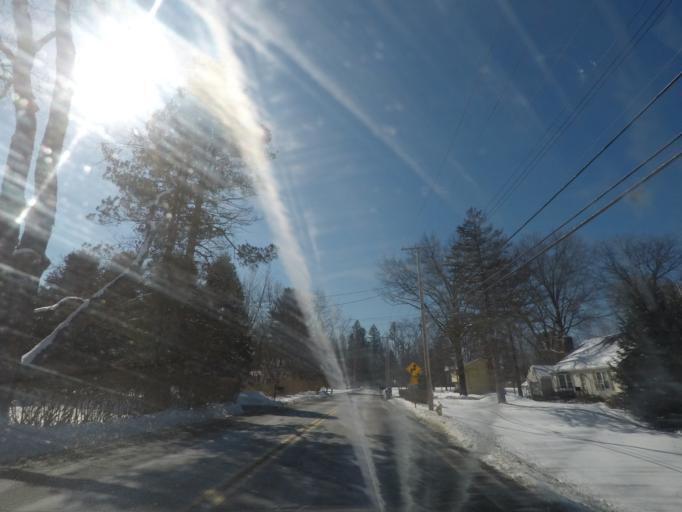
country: US
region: New York
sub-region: Schenectady County
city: Niskayuna
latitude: 42.7777
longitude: -73.8470
